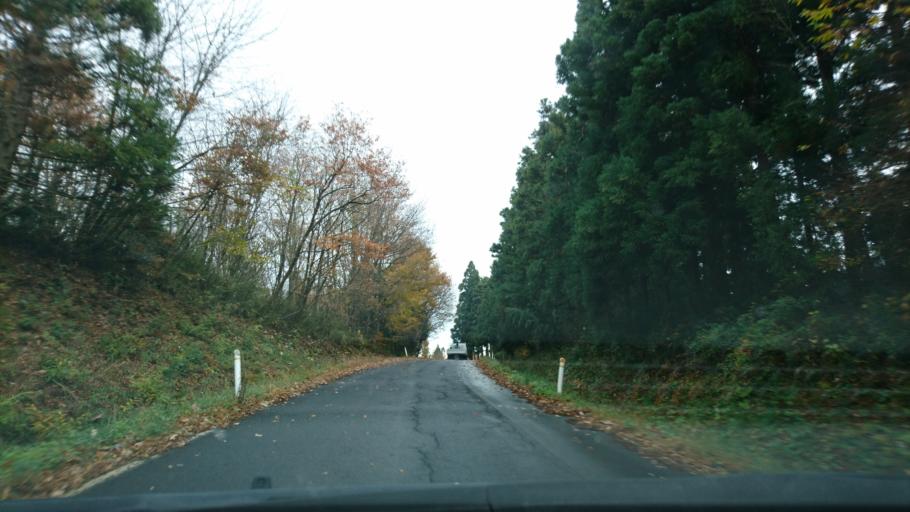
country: JP
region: Iwate
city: Ichinoseki
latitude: 38.8843
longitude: 141.1787
